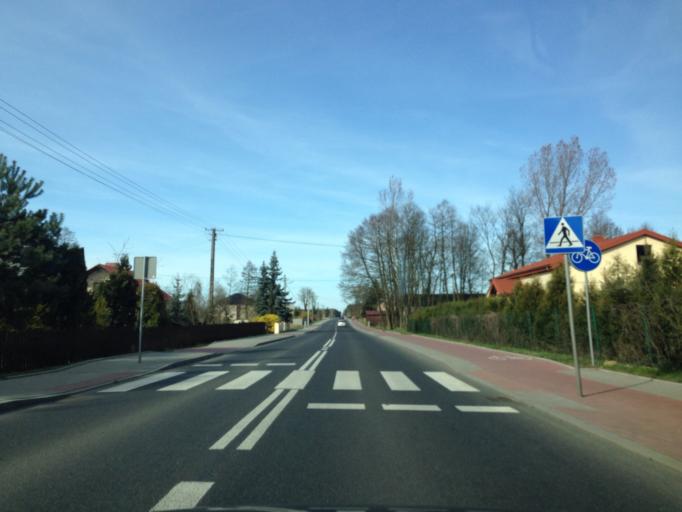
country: PL
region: Lodz Voivodeship
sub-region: Powiat poddebicki
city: Wartkowice
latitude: 51.9430
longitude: 18.9973
